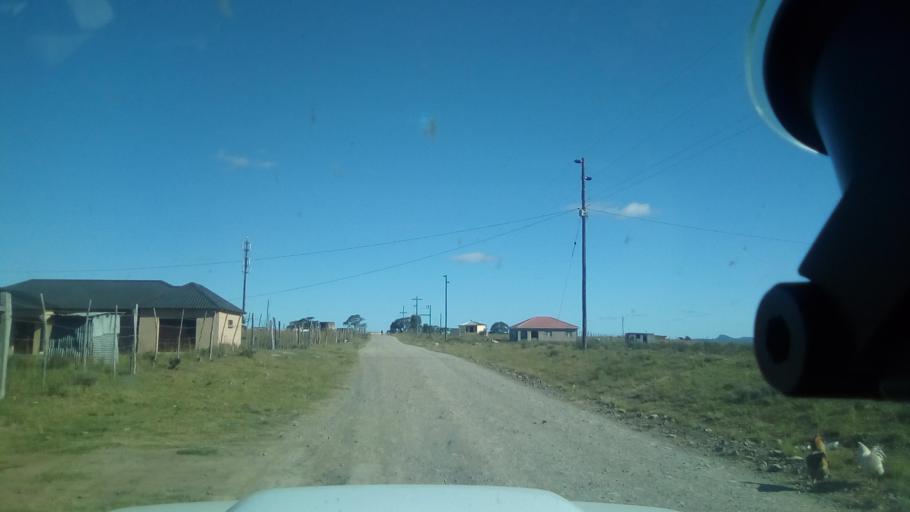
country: ZA
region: Eastern Cape
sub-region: Buffalo City Metropolitan Municipality
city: Bhisho
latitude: -32.7876
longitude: 27.3262
